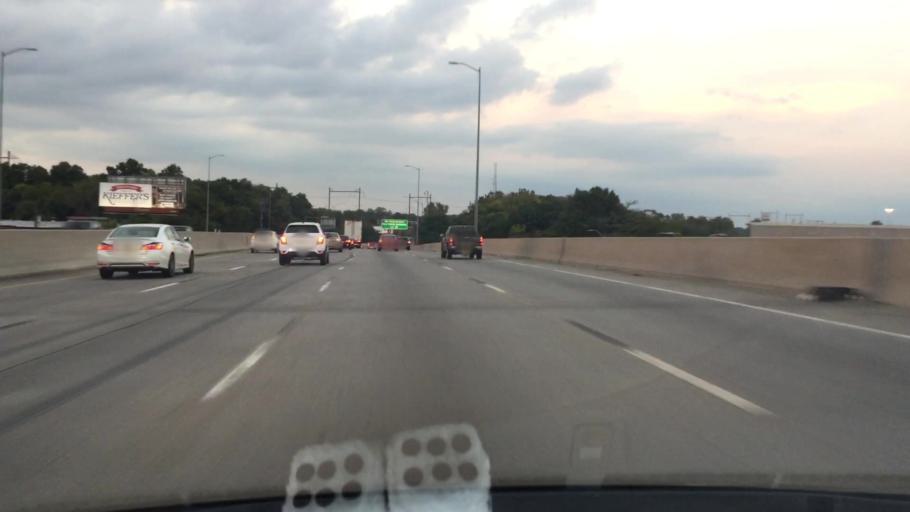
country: US
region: New Jersey
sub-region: Burlington County
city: Riverton
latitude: 40.0303
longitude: -75.0218
